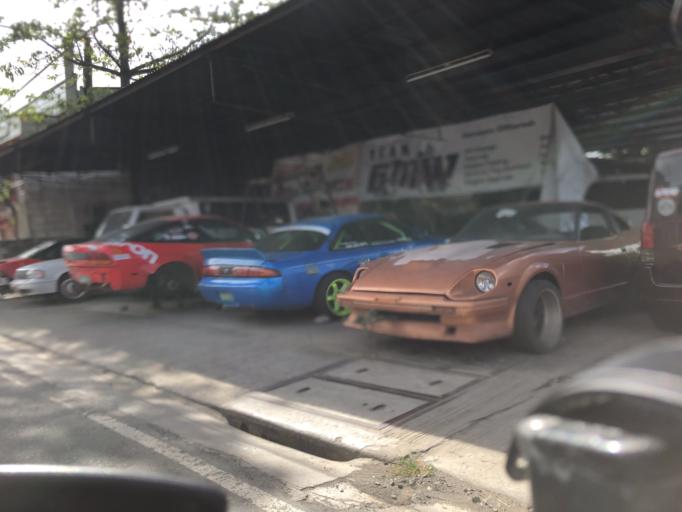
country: PH
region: Calabarzon
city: Bagong Pagasa
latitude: 14.7212
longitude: 121.0612
